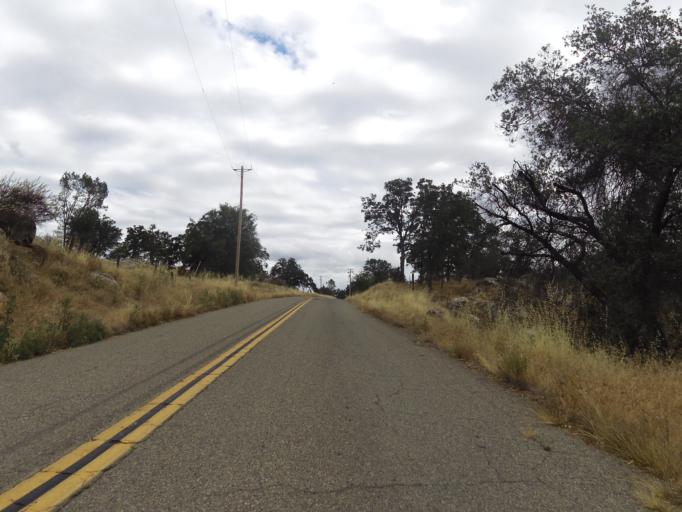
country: US
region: California
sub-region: Madera County
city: Yosemite Lakes
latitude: 37.2652
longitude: -119.8574
